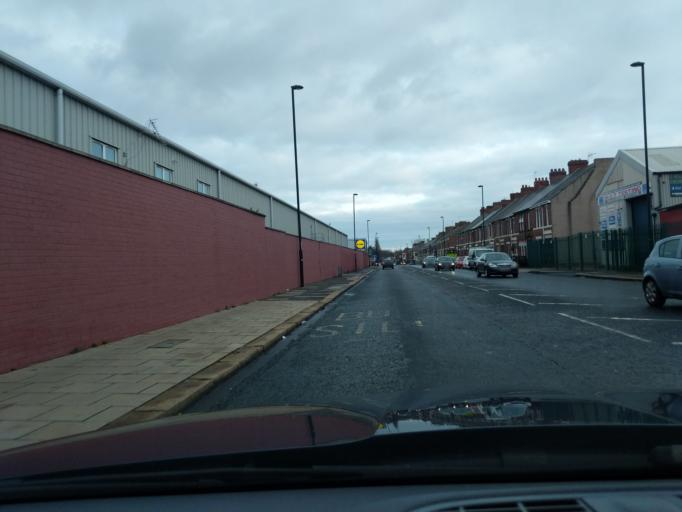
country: GB
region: England
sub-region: Borough of North Tyneside
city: Wallsend
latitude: 54.9834
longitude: -1.5637
